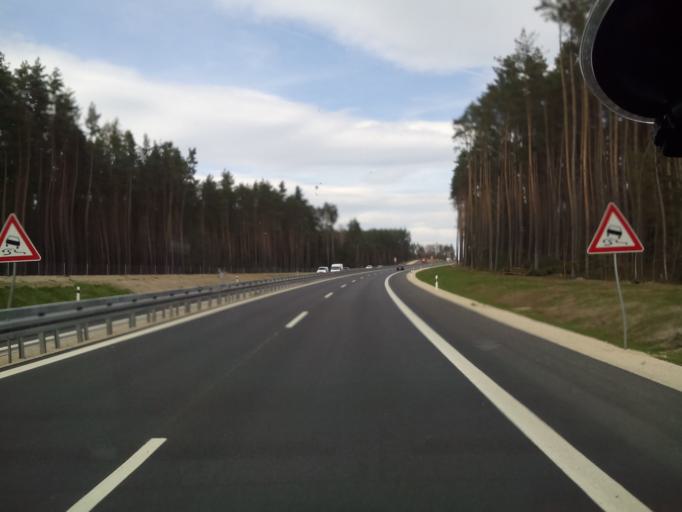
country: DE
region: Bavaria
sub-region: Regierungsbezirk Mittelfranken
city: Roth
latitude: 49.2130
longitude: 11.0762
